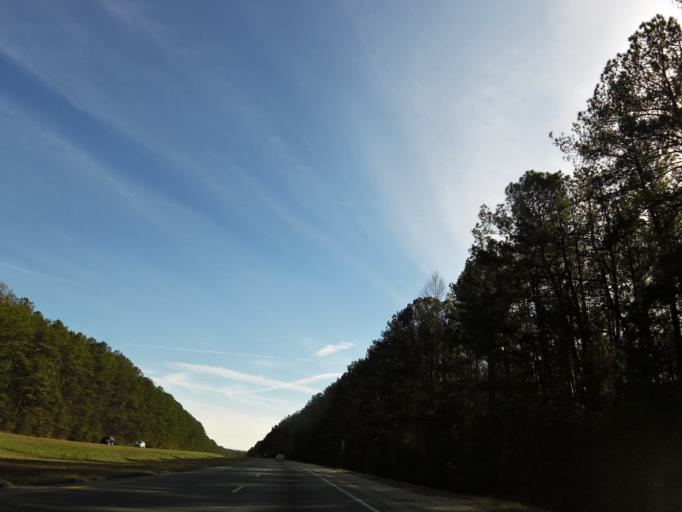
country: US
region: Georgia
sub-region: Harris County
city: Hamilton
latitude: 32.7698
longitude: -85.0206
